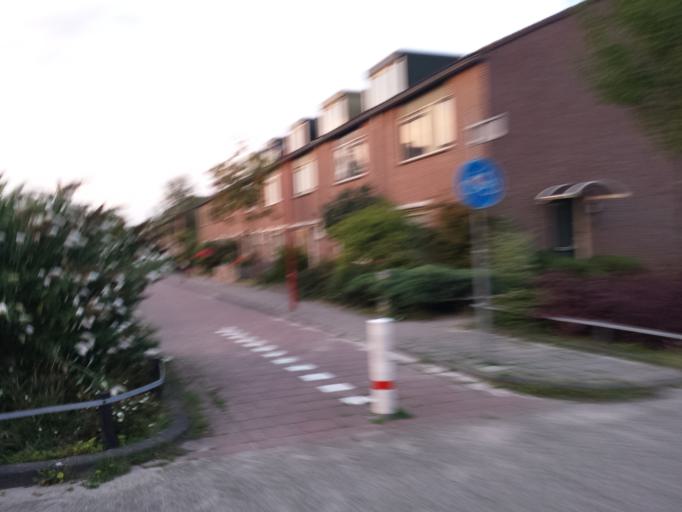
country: NL
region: South Holland
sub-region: Gemeente Zoetermeer
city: Zoetermeer
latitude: 52.0413
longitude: 4.4848
